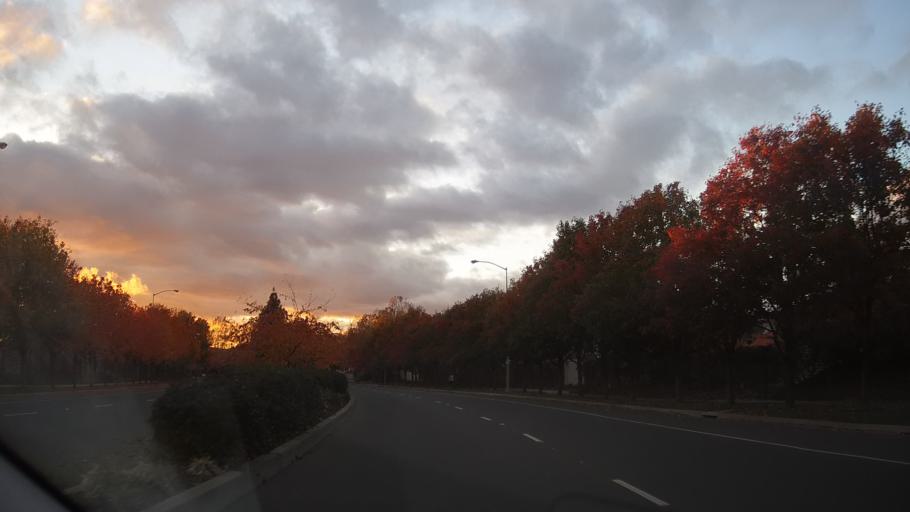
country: US
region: California
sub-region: Solano County
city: Fairfield
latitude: 38.2927
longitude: -122.0165
